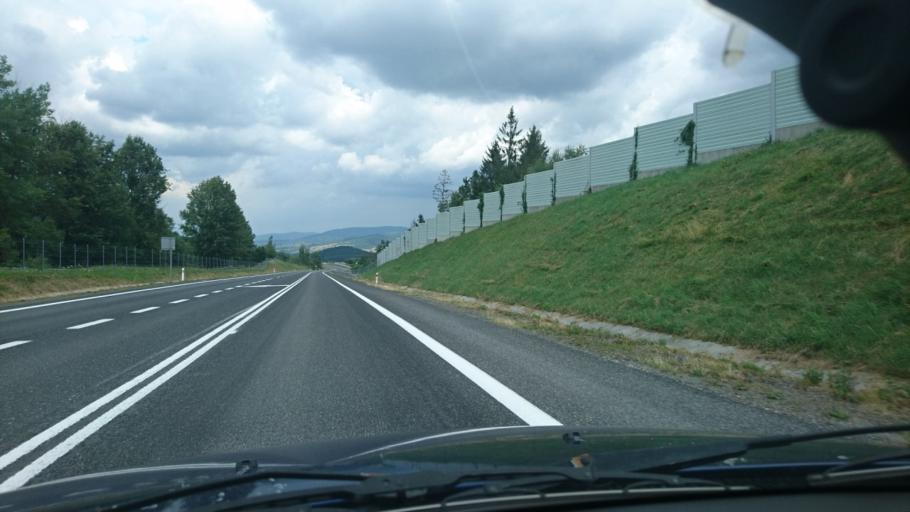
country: PL
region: Silesian Voivodeship
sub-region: Powiat zywiecki
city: Kamesznica
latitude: 49.5486
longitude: 19.0351
